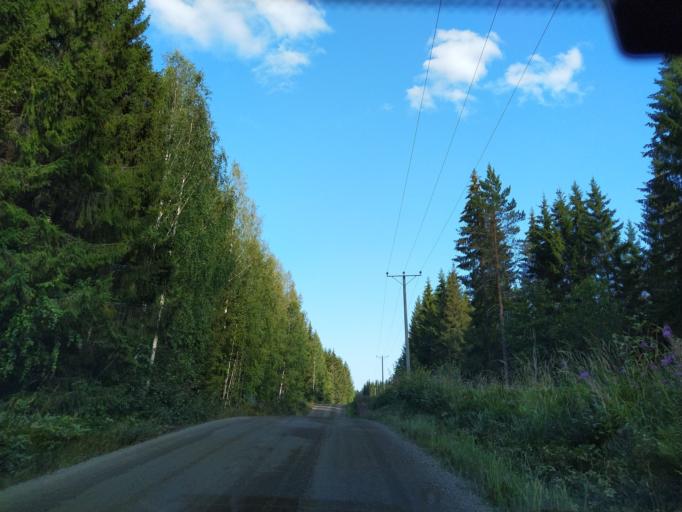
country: FI
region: Central Finland
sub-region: Jaemsae
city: Kuhmoinen
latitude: 61.6925
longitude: 24.9493
